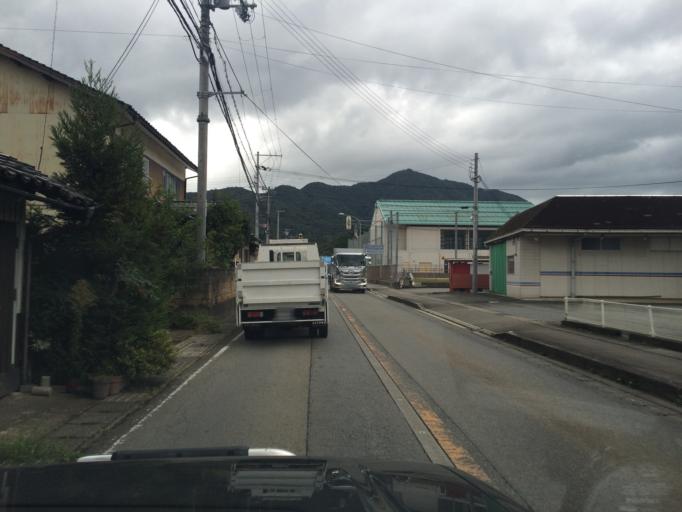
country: JP
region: Hyogo
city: Toyooka
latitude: 35.4303
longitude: 134.7953
